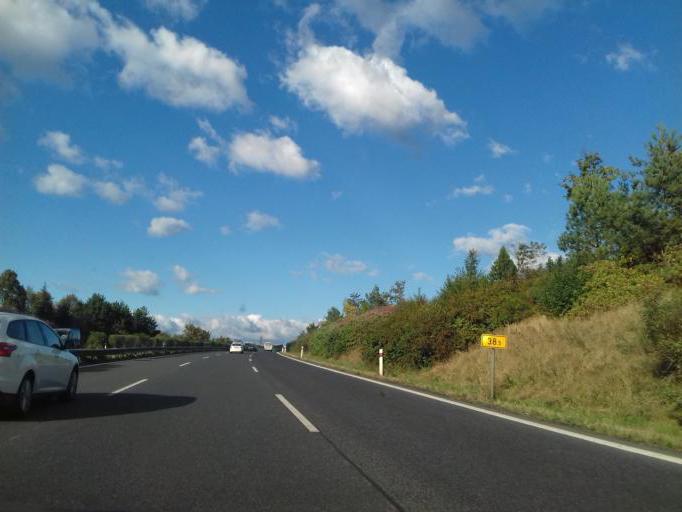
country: CZ
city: Ohrazenice
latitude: 50.6276
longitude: 15.1087
